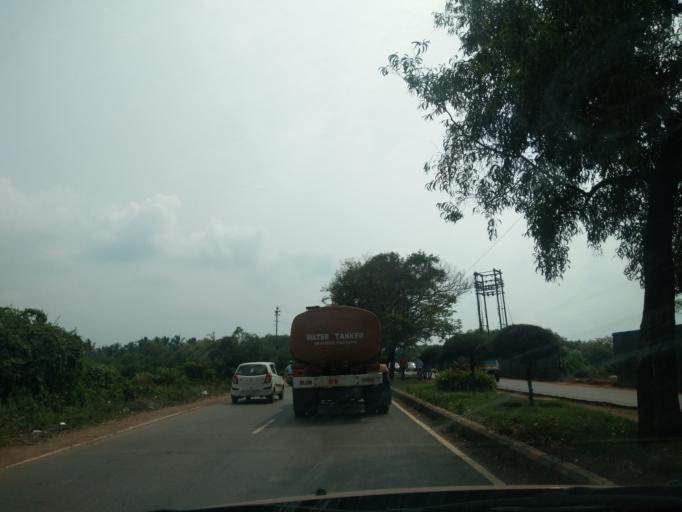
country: IN
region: Goa
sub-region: North Goa
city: Panaji
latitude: 15.4933
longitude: 73.8412
